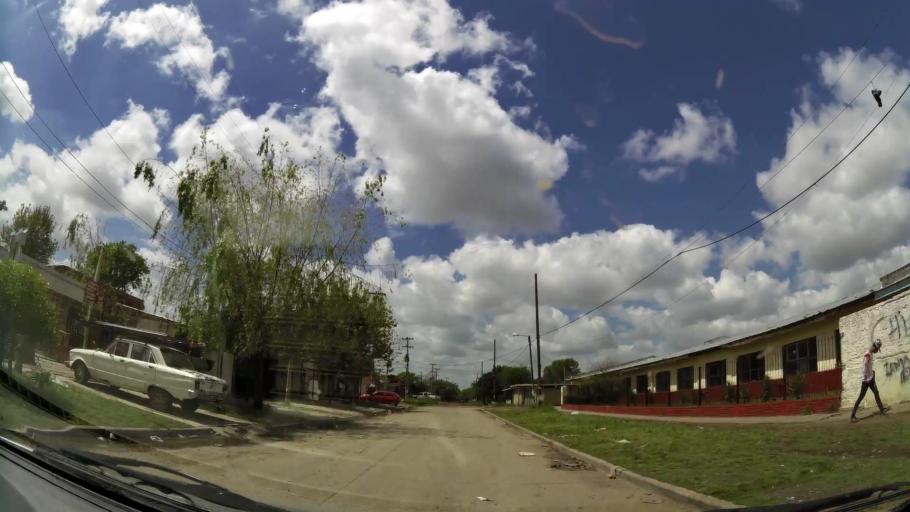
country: AR
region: Buenos Aires
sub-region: Partido de Quilmes
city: Quilmes
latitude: -34.8399
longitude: -58.2319
